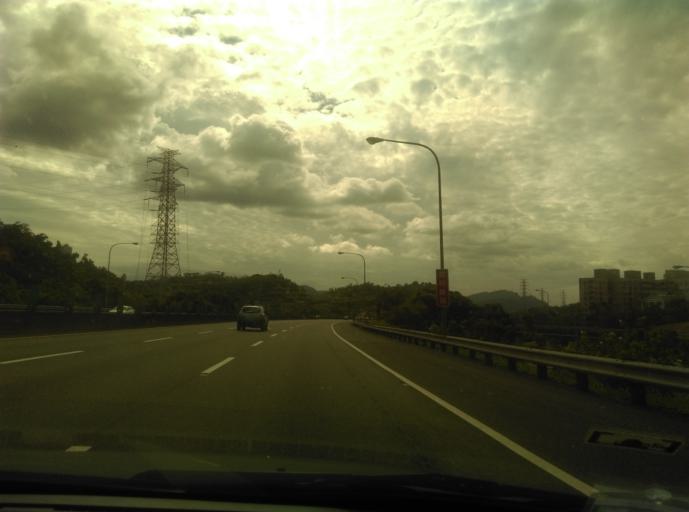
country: TW
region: Taipei
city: Taipei
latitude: 25.0579
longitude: 121.6401
